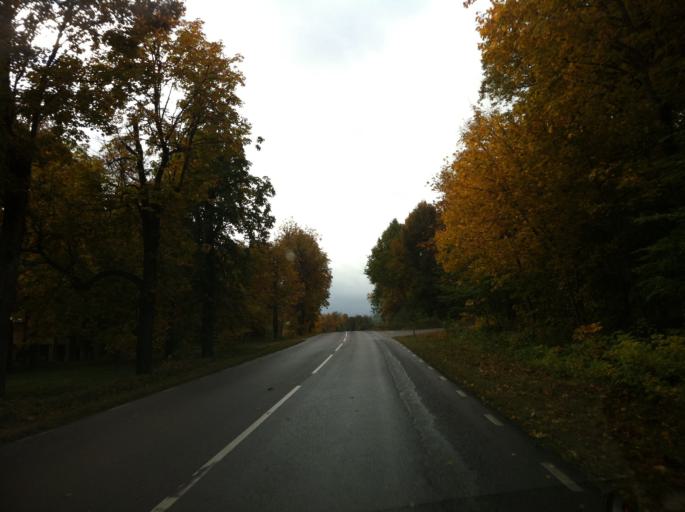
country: SE
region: OEstergoetland
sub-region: Linkopings Kommun
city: Malmslatt
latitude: 58.3797
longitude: 15.5546
